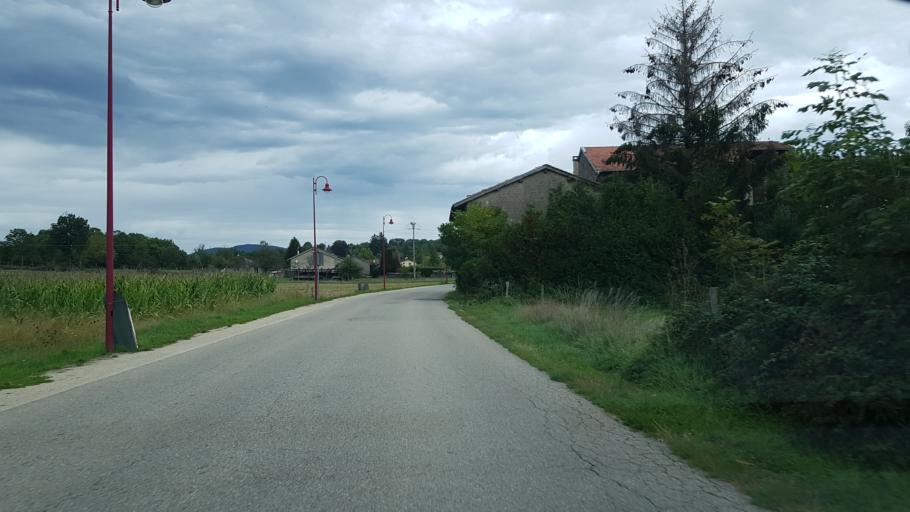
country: FR
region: Rhone-Alpes
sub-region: Departement de l'Ain
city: Villereversure
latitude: 46.2280
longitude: 5.4175
